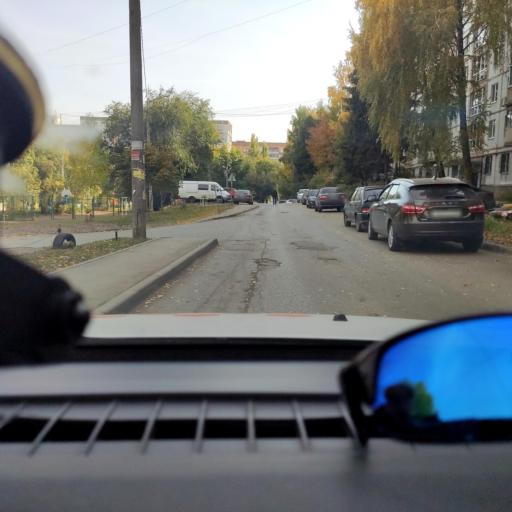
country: RU
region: Samara
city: Samara
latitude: 53.2381
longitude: 50.2216
